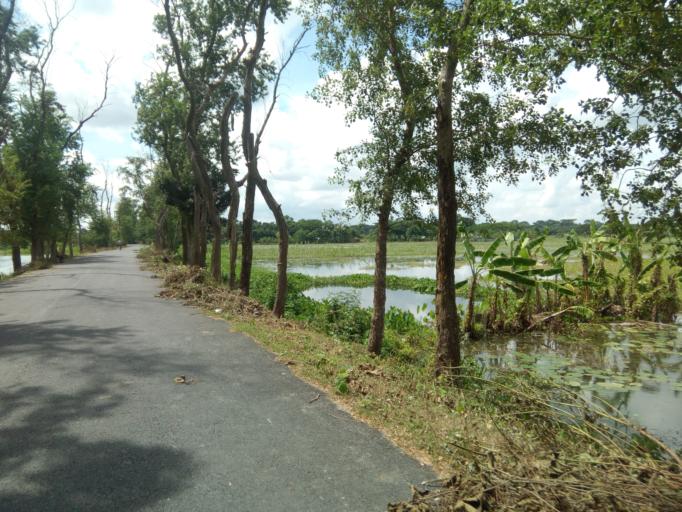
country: BD
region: Khulna
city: Kalia
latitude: 23.0141
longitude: 89.7242
